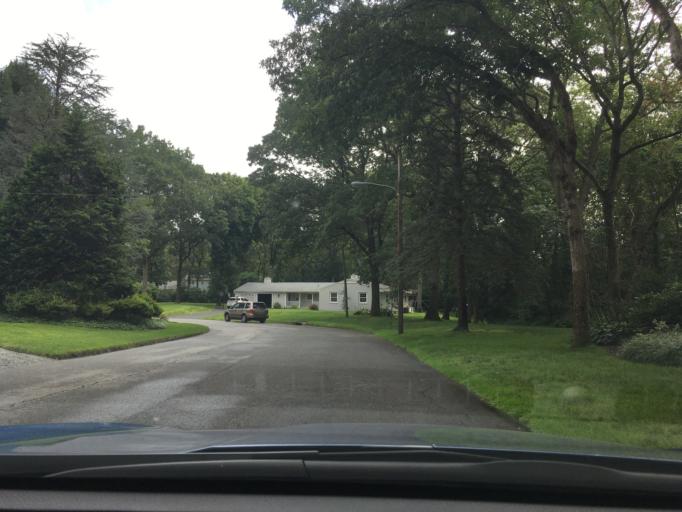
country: US
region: Rhode Island
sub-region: Kent County
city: East Greenwich
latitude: 41.6423
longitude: -71.4783
